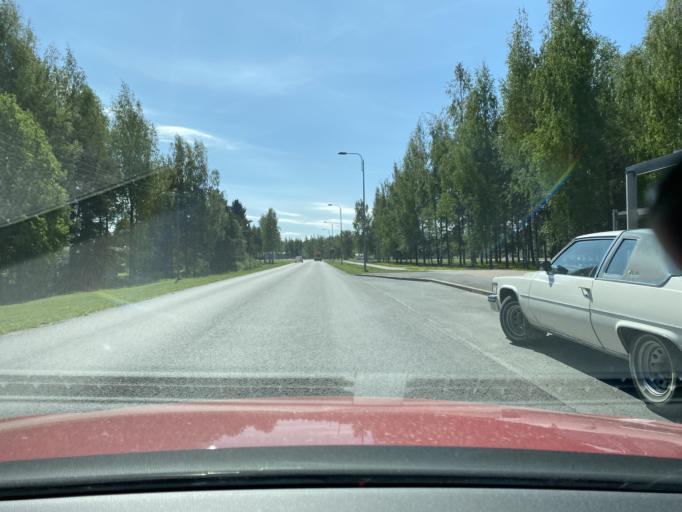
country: FI
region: Satakunta
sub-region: Rauma
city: Eura
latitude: 61.1287
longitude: 22.1447
